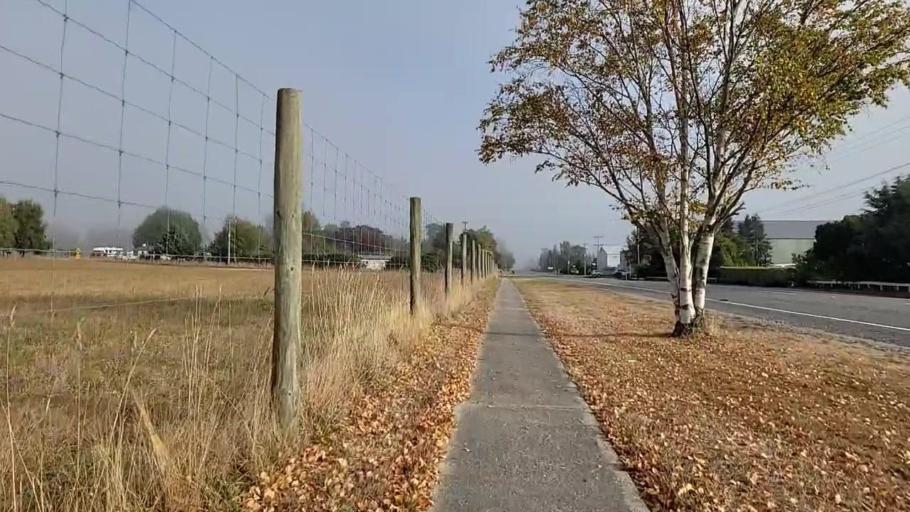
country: NZ
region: Southland
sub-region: Gore District
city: Gore
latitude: -45.6368
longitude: 169.3670
